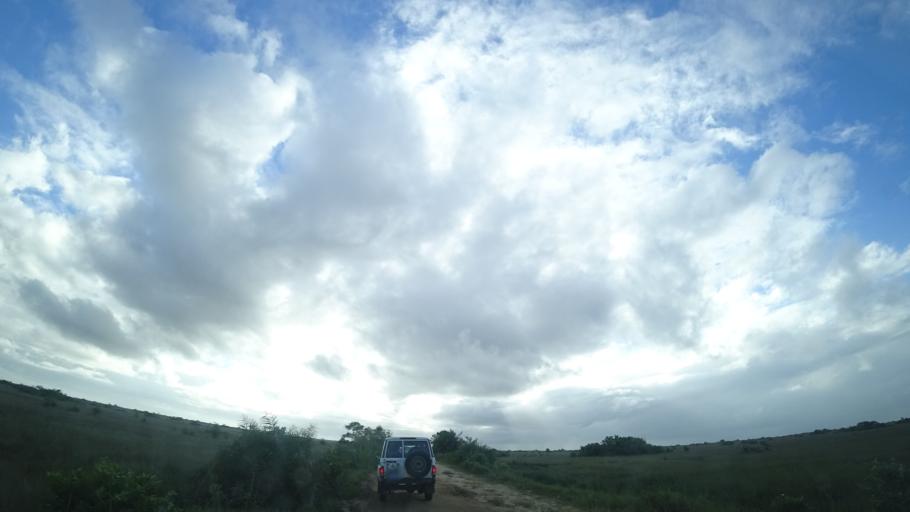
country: MZ
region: Sofala
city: Beira
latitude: -19.7060
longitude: 35.0187
